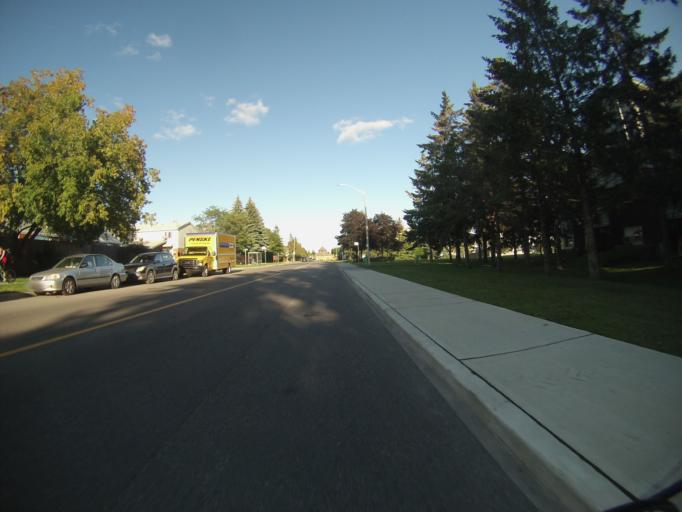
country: CA
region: Ontario
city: Ottawa
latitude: 45.3651
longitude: -75.6311
